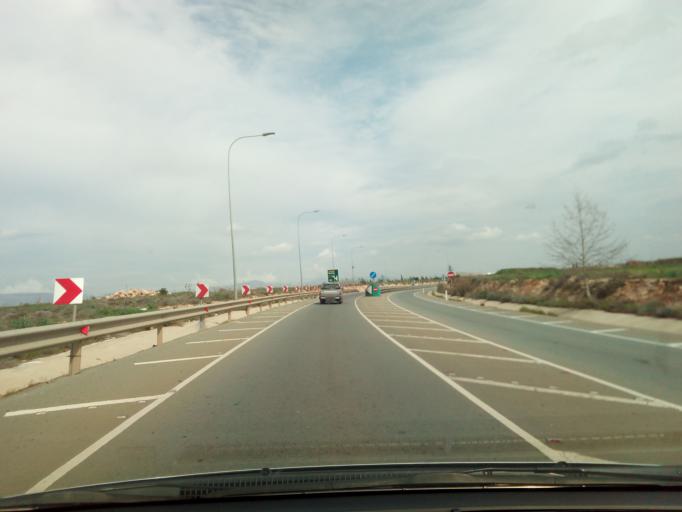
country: CY
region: Lefkosia
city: Kokkinotrimithia
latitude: 35.1614
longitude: 33.1612
